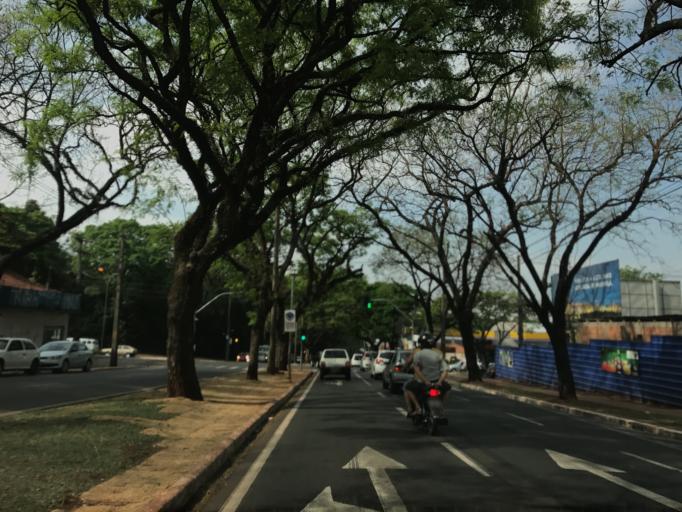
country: BR
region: Parana
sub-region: Maringa
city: Maringa
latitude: -23.4340
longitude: -51.9295
